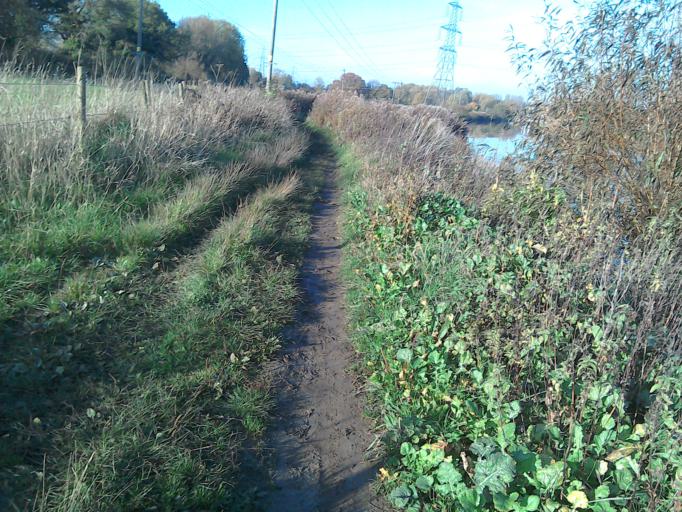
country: GB
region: England
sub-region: Oxfordshire
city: Radley
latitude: 51.7030
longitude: -1.2333
